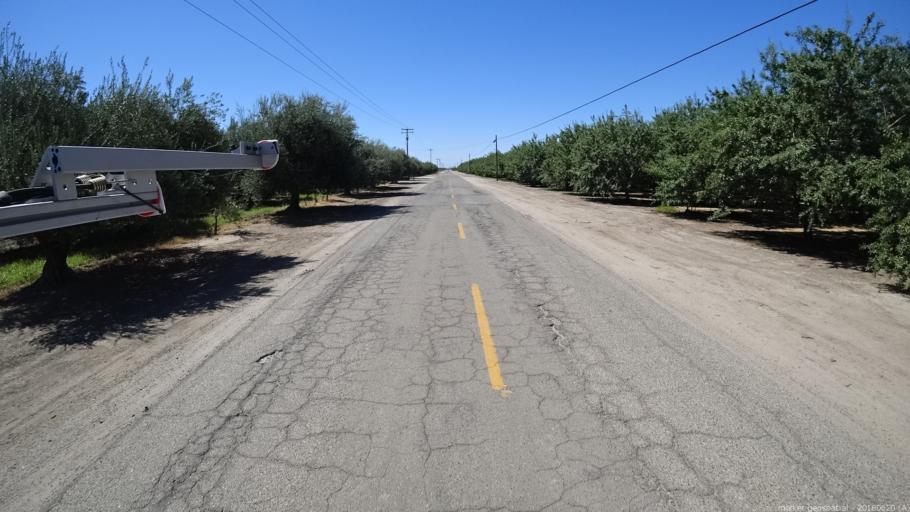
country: US
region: California
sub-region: Madera County
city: Parkwood
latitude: 36.9082
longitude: -120.0104
